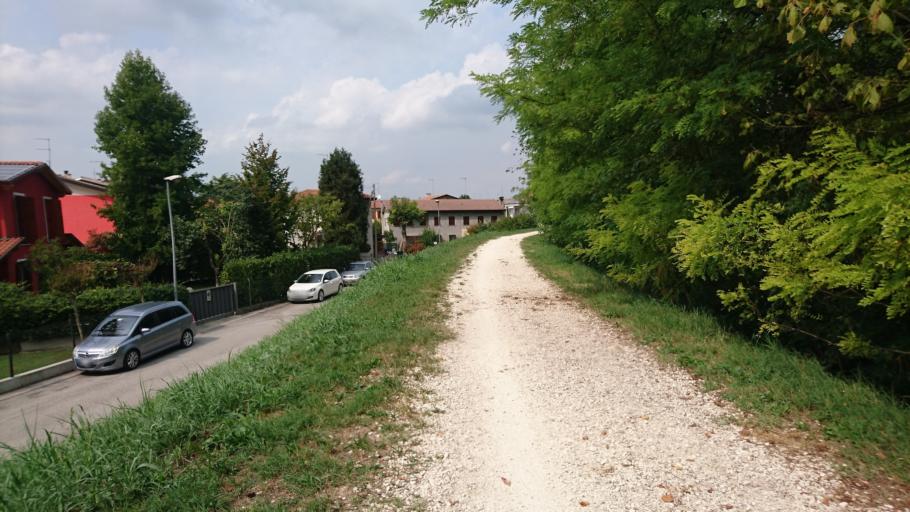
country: IT
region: Veneto
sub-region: Provincia di Padova
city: Limena
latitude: 45.4724
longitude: 11.8487
